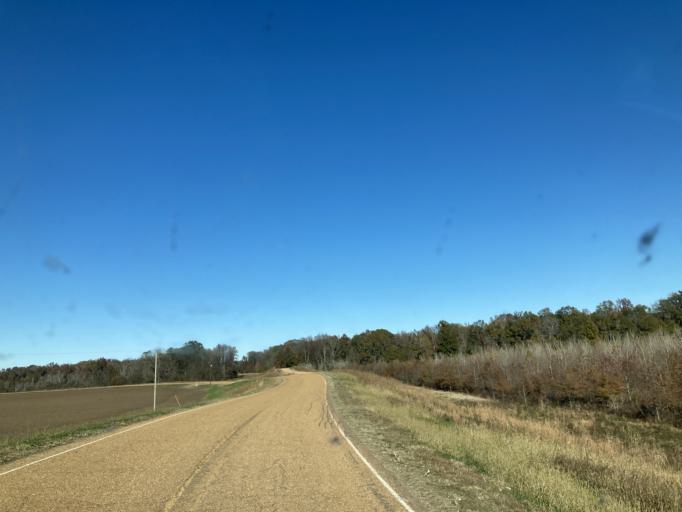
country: US
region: Mississippi
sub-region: Yazoo County
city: Yazoo City
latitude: 32.7774
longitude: -90.6375
